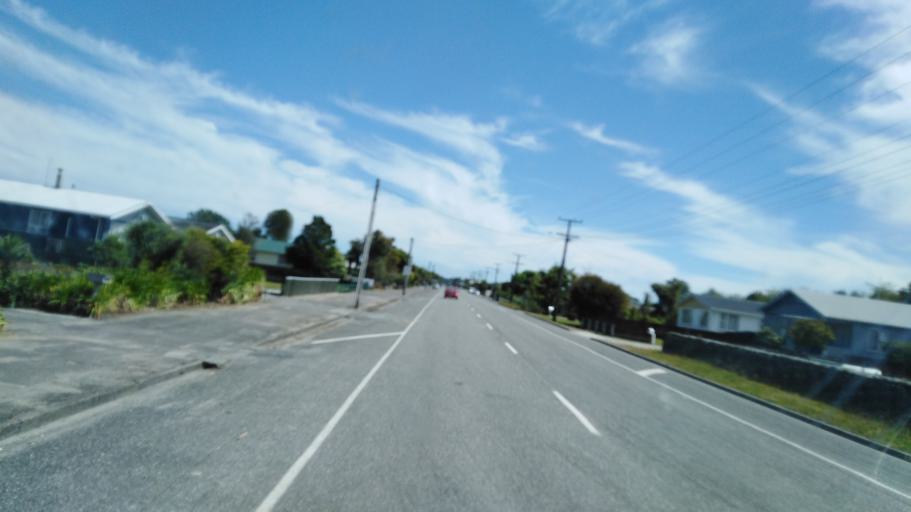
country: NZ
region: West Coast
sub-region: Buller District
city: Westport
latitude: -41.7534
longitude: 171.6148
